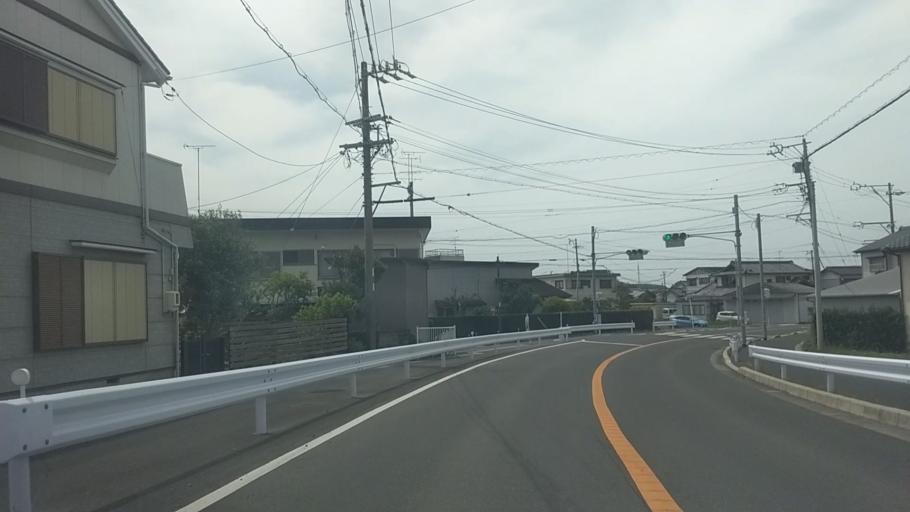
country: JP
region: Shizuoka
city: Kosai-shi
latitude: 34.7350
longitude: 137.5381
